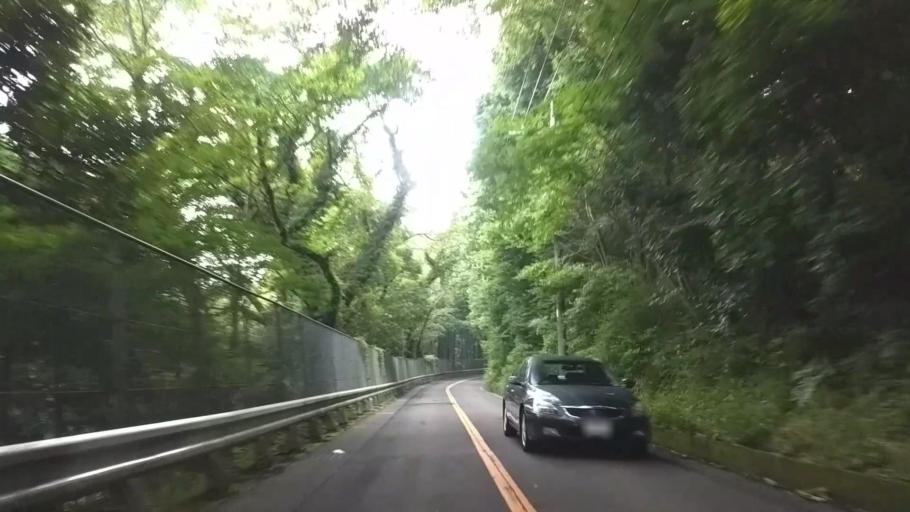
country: JP
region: Kanagawa
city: Ninomiya
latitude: 35.3361
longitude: 139.2371
